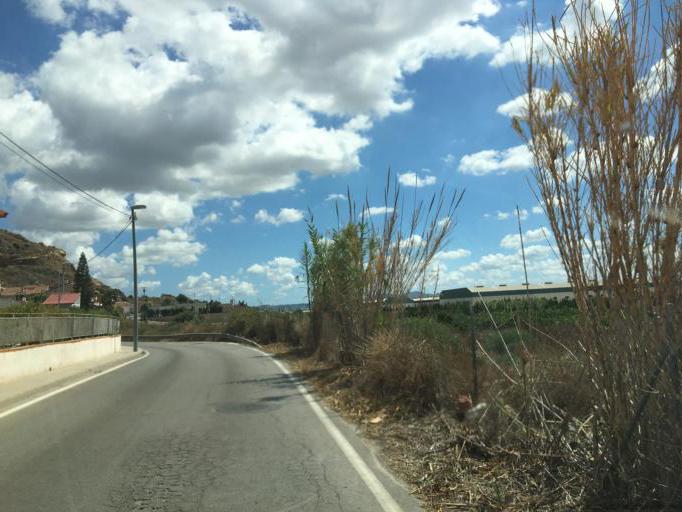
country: ES
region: Murcia
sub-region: Murcia
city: Santomera
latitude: 38.0526
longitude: -1.0618
